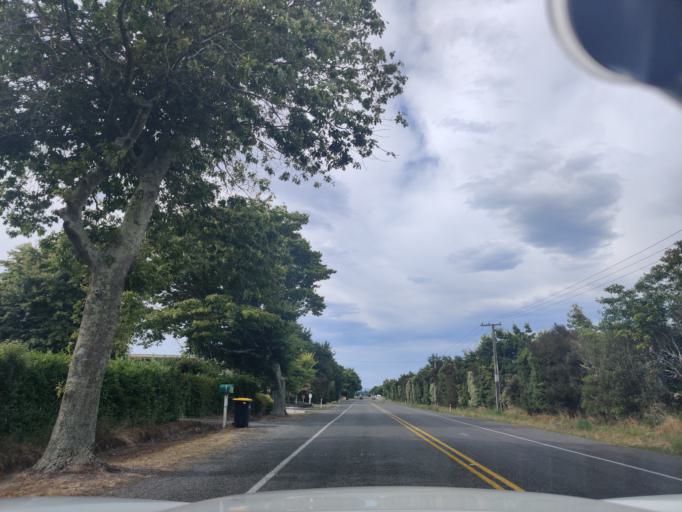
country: NZ
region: Wellington
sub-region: Masterton District
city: Masterton
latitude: -40.9315
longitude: 175.6719
